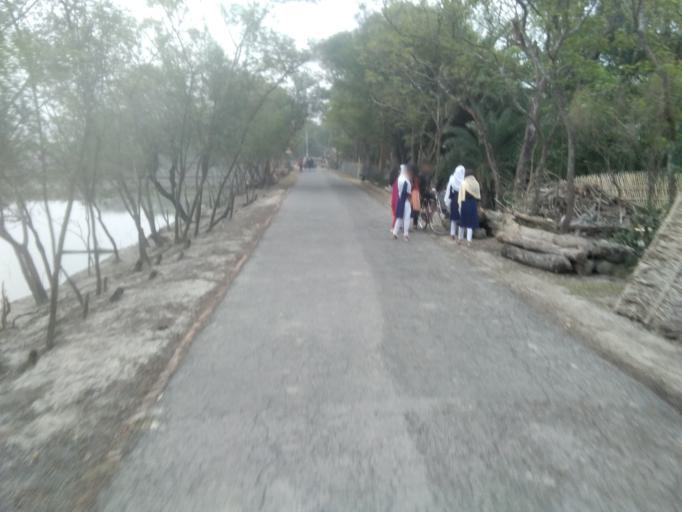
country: BD
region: Khulna
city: Satkhira
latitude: 22.5787
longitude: 89.0706
